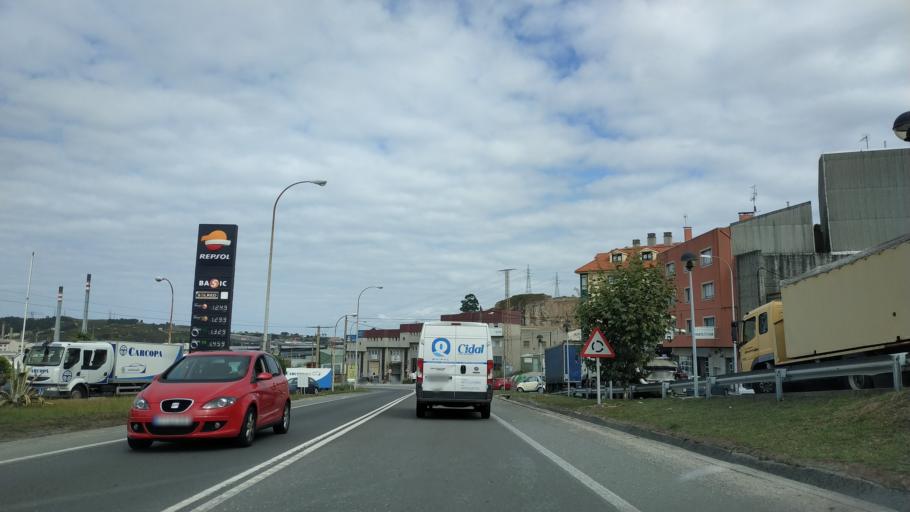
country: ES
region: Galicia
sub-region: Provincia da Coruna
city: A Coruna
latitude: 43.3399
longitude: -8.4452
